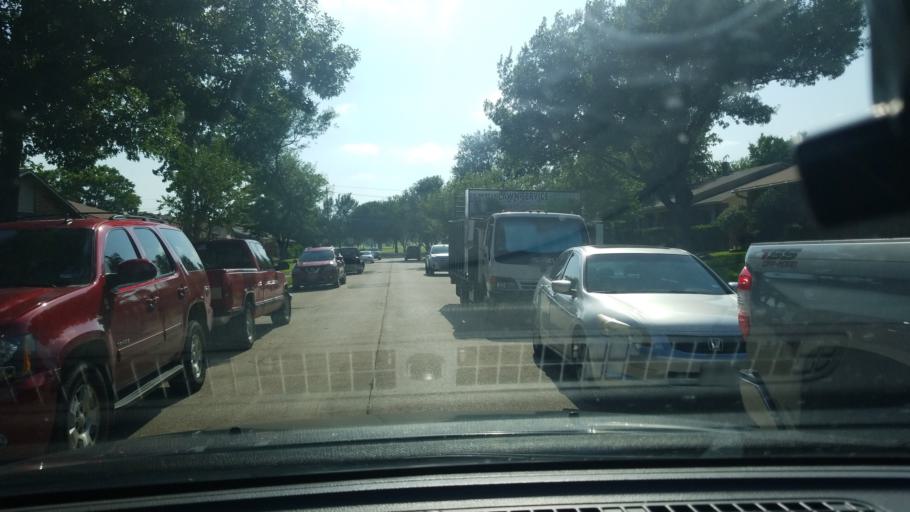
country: US
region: Texas
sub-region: Dallas County
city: Sunnyvale
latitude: 32.8182
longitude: -96.6058
